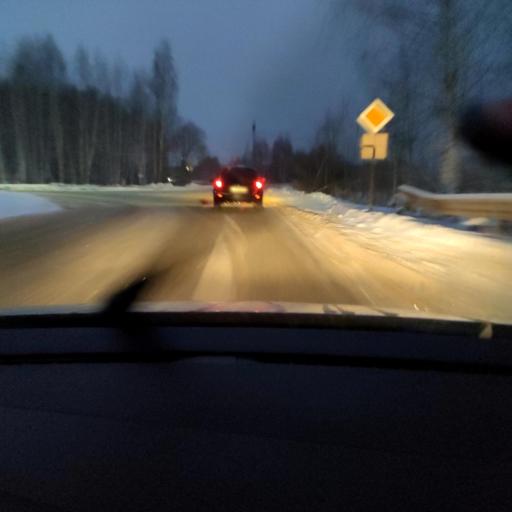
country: RU
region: Tatarstan
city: Aysha
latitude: 55.8709
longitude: 48.5793
